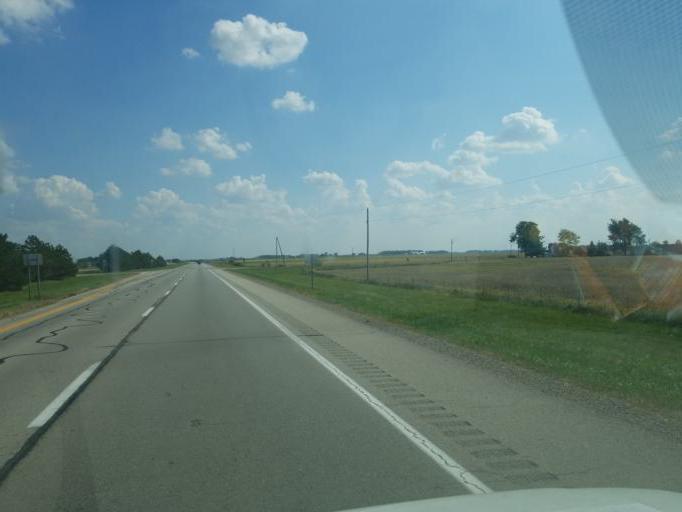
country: US
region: Ohio
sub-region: Van Wert County
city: Convoy
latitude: 40.9780
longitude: -84.7660
